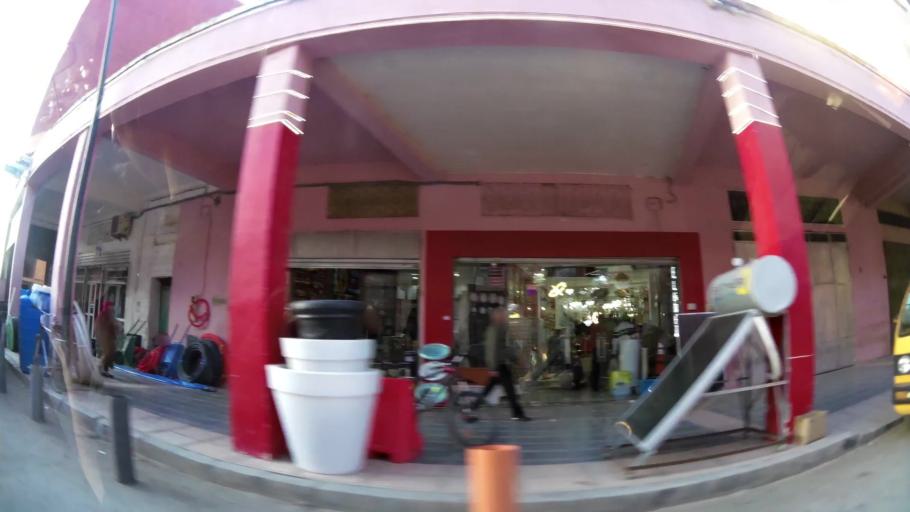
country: MA
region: Oriental
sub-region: Berkane-Taourirt
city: Berkane
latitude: 34.9225
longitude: -2.3353
